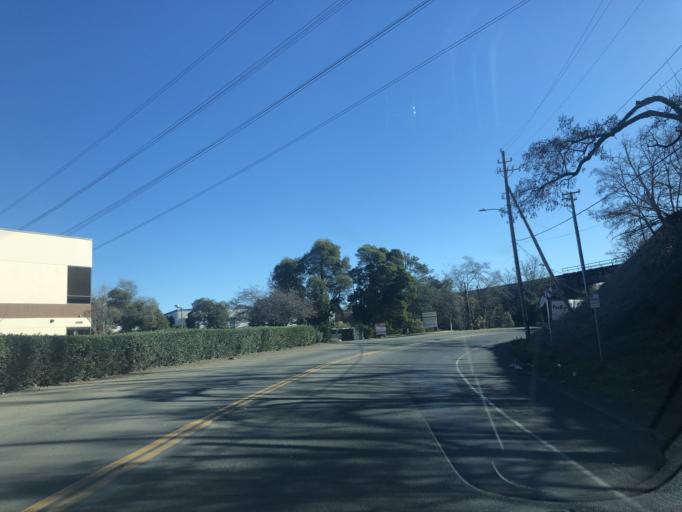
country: US
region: California
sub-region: Contra Costa County
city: Vine Hill
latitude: 38.0053
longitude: -122.0869
